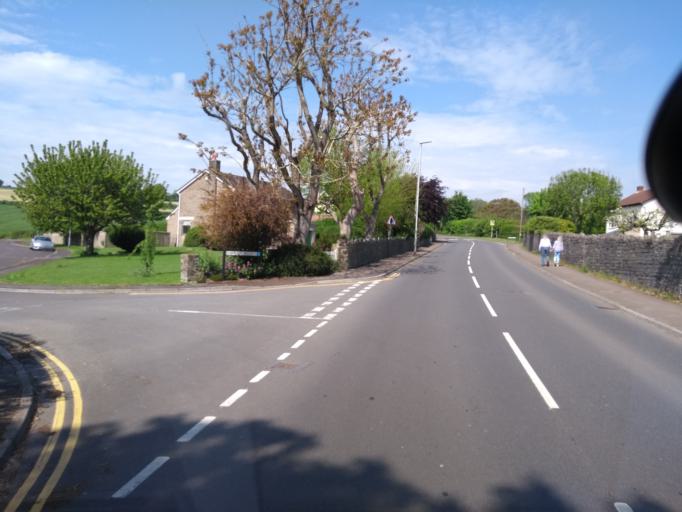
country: GB
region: England
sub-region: Somerset
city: Chard
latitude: 50.8730
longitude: -2.9733
